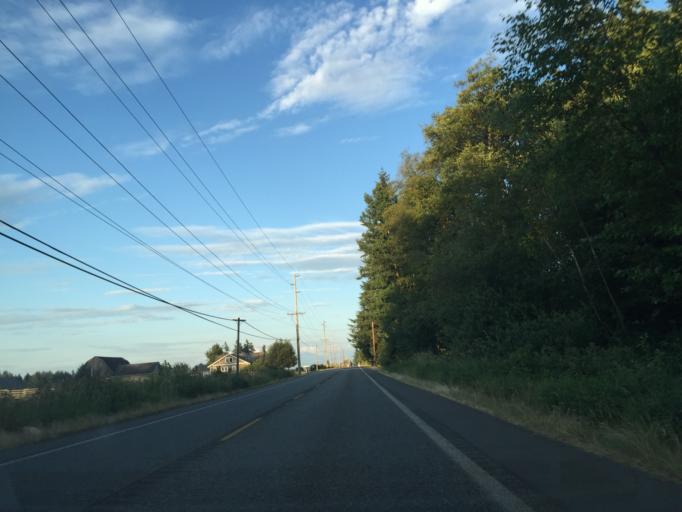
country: US
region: Washington
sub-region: Whatcom County
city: Ferndale
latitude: 48.9355
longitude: -122.6050
